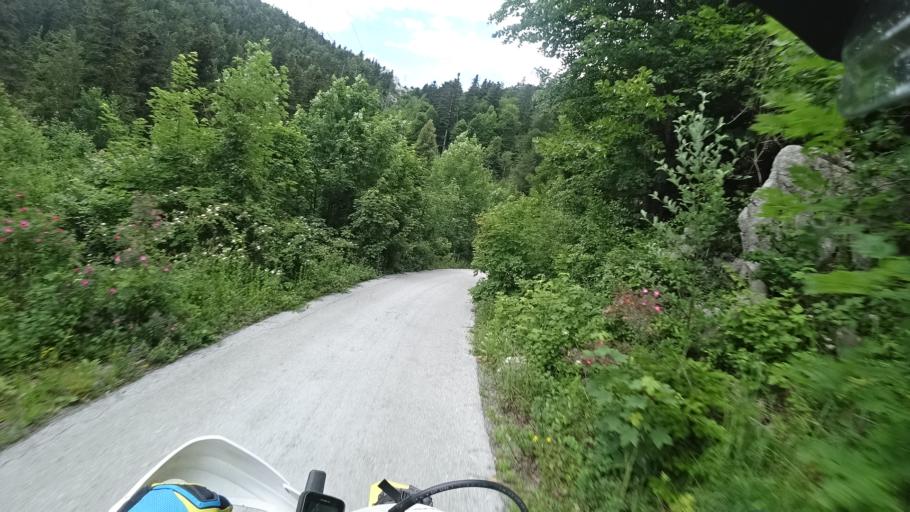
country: HR
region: Primorsko-Goranska
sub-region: Grad Crikvenica
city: Crikvenica
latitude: 45.2636
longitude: 14.7106
